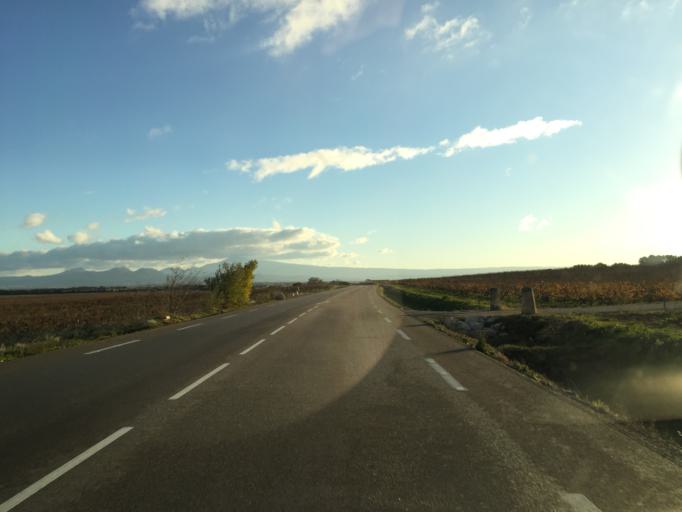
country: FR
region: Provence-Alpes-Cote d'Azur
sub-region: Departement du Vaucluse
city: Courthezon
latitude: 44.0967
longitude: 4.8465
